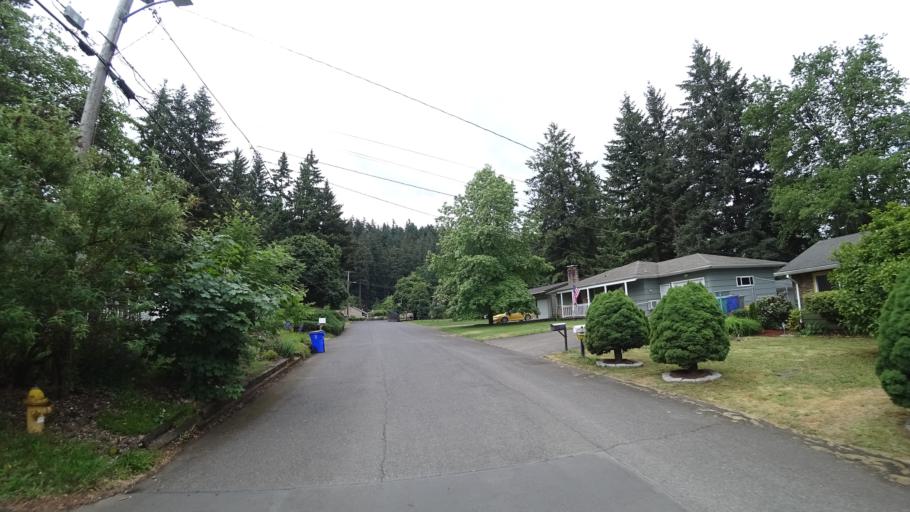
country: US
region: Oregon
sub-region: Clackamas County
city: Happy Valley
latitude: 45.4946
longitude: -122.5097
